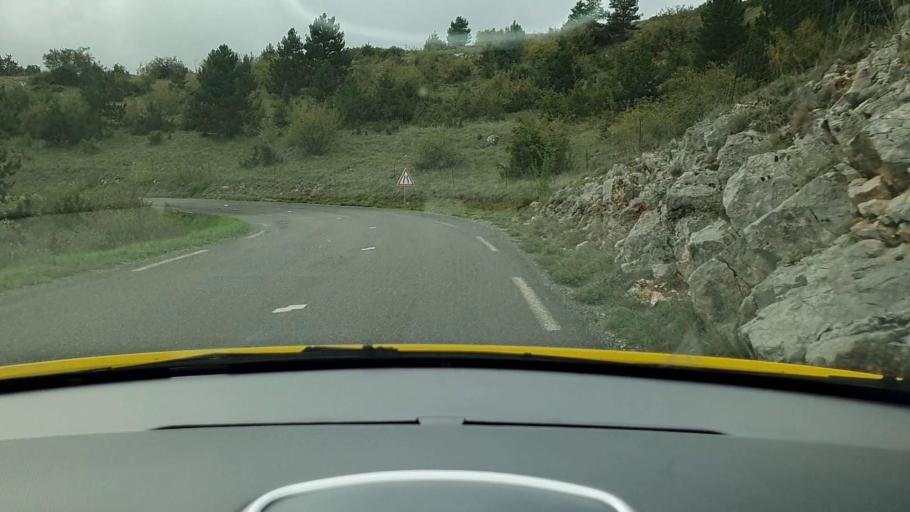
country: FR
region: Languedoc-Roussillon
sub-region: Departement de la Lozere
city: Meyrueis
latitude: 44.0965
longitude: 3.3705
